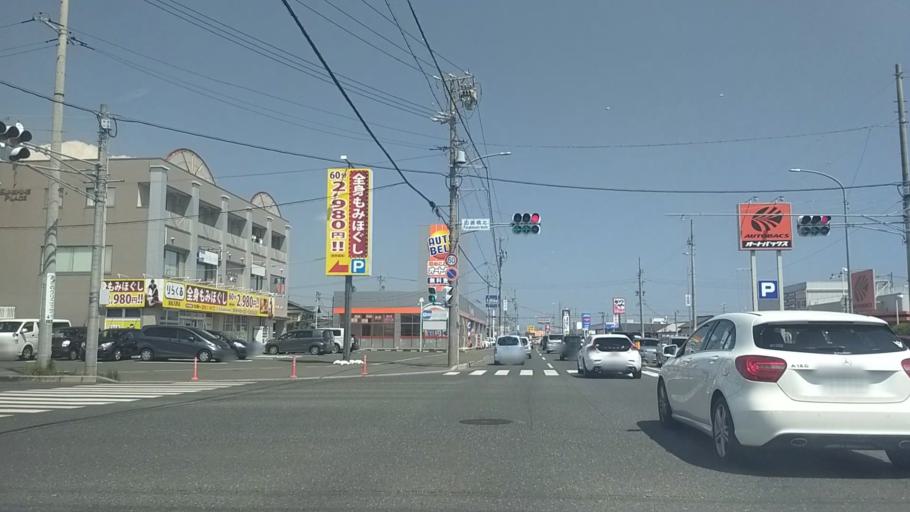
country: JP
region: Shizuoka
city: Hamamatsu
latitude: 34.6981
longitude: 137.6790
